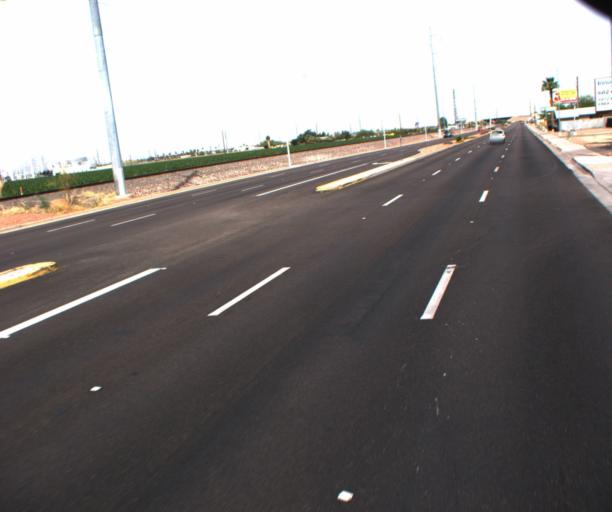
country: US
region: Arizona
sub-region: Maricopa County
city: Glendale
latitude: 33.5563
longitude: -112.2069
